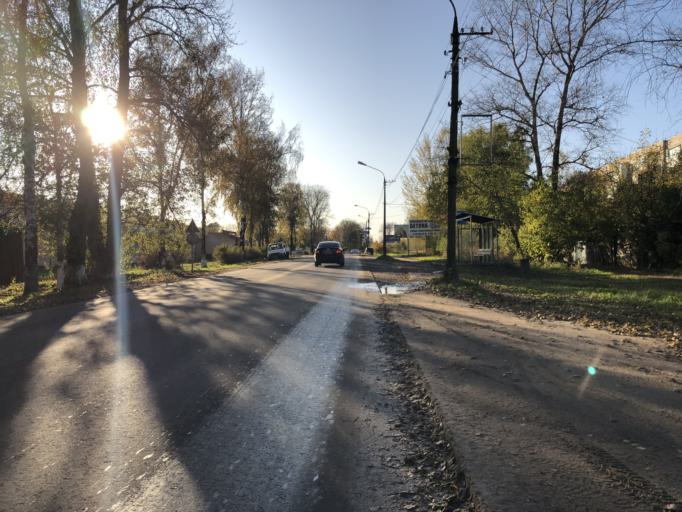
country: RU
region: Tverskaya
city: Rzhev
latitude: 56.2465
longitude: 34.3378
